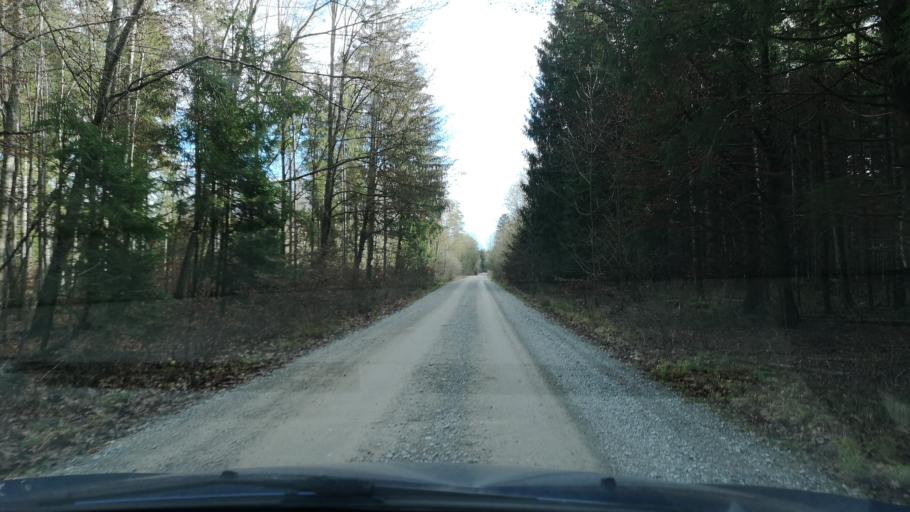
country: DE
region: Bavaria
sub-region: Upper Bavaria
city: Anzing
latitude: 48.1323
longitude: 11.8846
